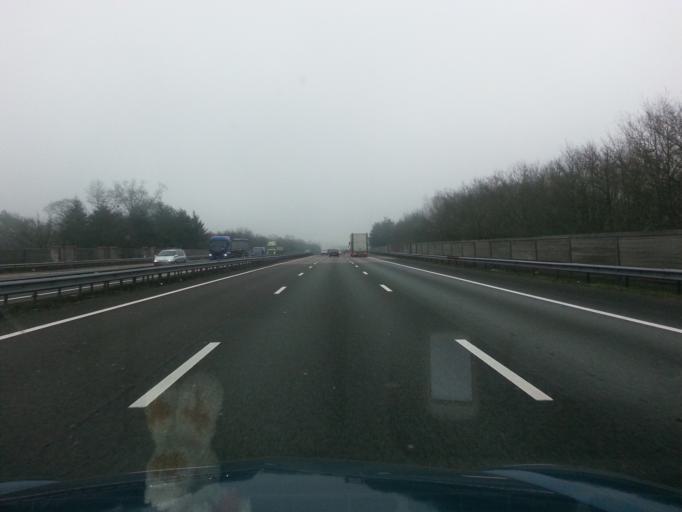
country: NL
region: Gelderland
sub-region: Gemeente Arnhem
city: Hoogkamp
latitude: 52.0263
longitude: 5.8711
